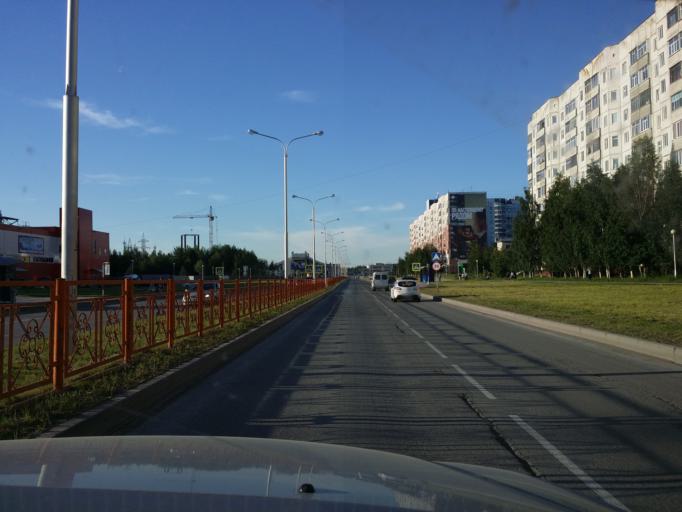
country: RU
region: Khanty-Mansiyskiy Avtonomnyy Okrug
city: Nizhnevartovsk
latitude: 60.9473
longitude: 76.6042
